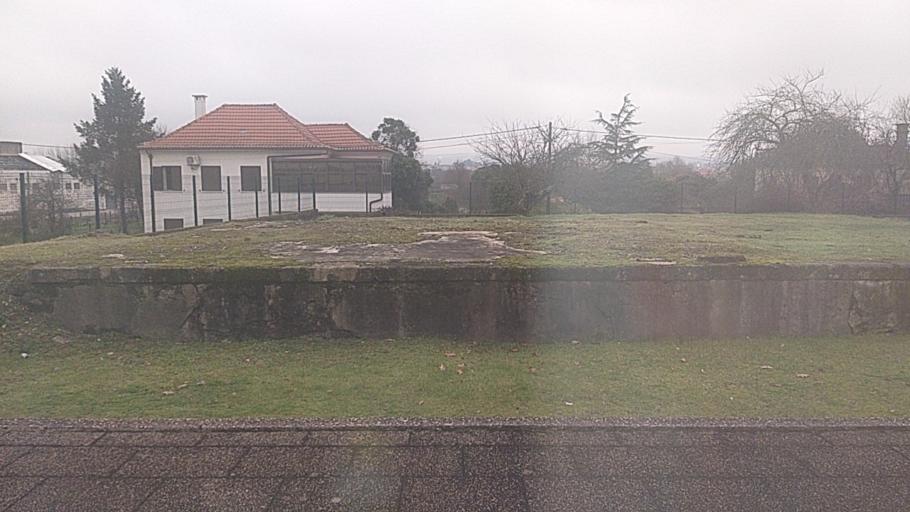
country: PT
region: Viseu
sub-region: Mortagua
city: Mortagua
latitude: 40.3913
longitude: -8.2417
